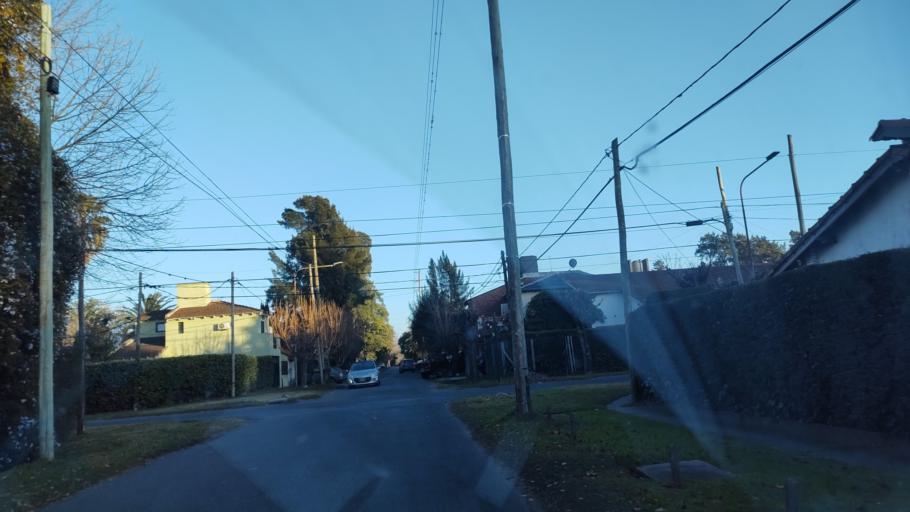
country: AR
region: Buenos Aires
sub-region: Partido de La Plata
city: La Plata
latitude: -34.8881
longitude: -58.0385
